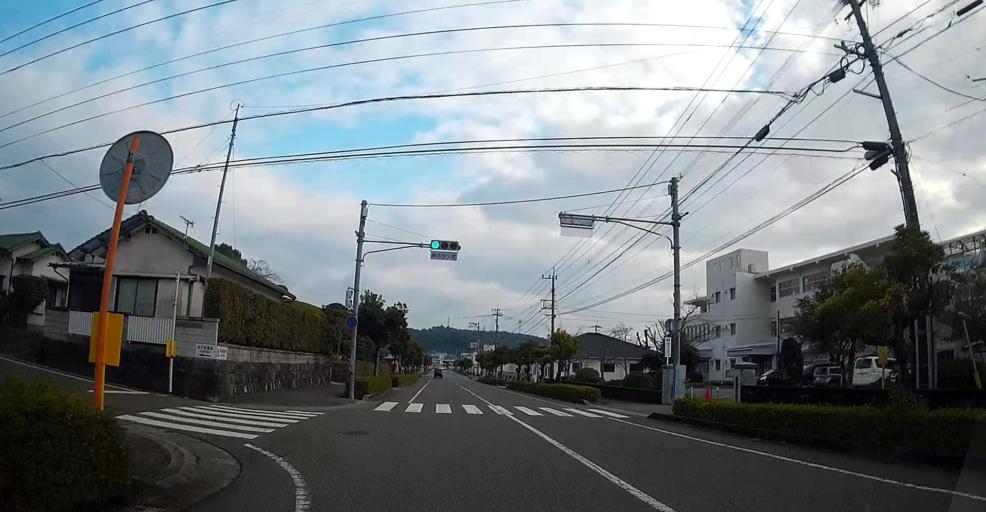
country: JP
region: Kumamoto
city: Hondo
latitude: 32.4634
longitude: 130.1867
